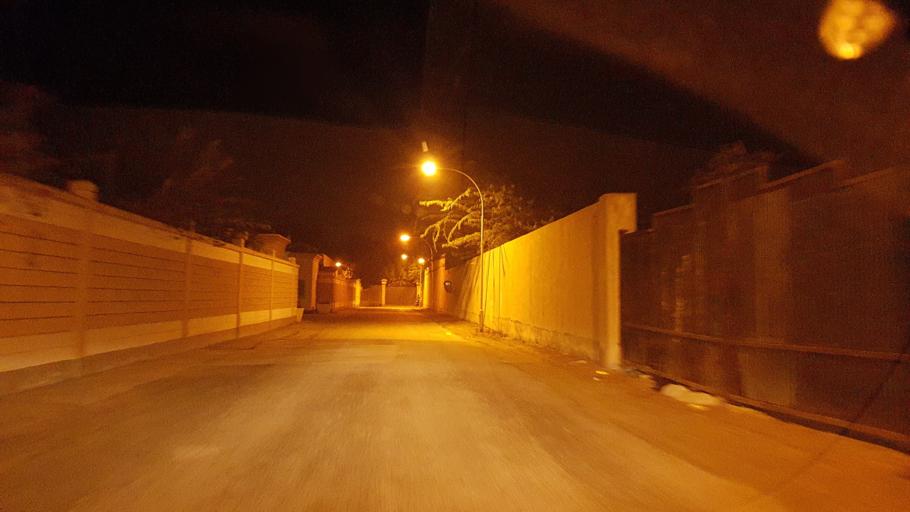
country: BH
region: Manama
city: Jidd Hafs
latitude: 26.2207
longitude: 50.4938
